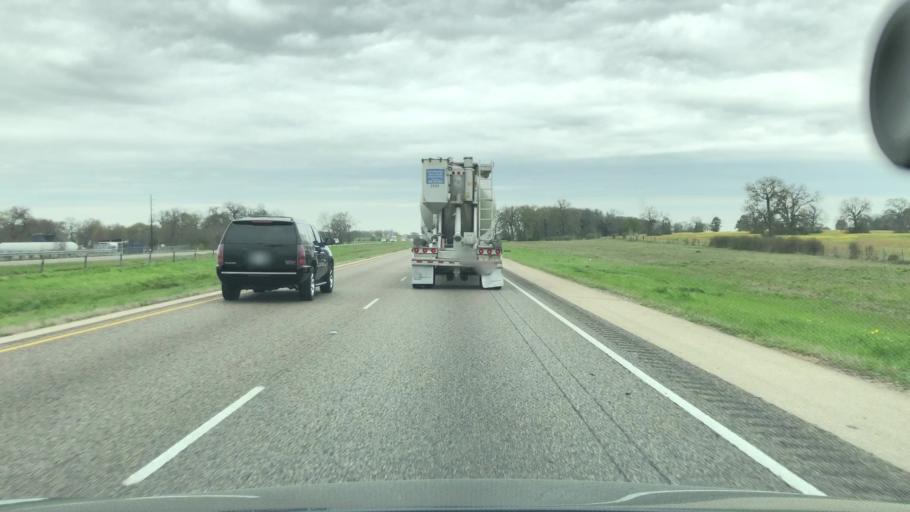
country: US
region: Texas
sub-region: Madison County
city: Madisonville
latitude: 31.0614
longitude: -95.9505
